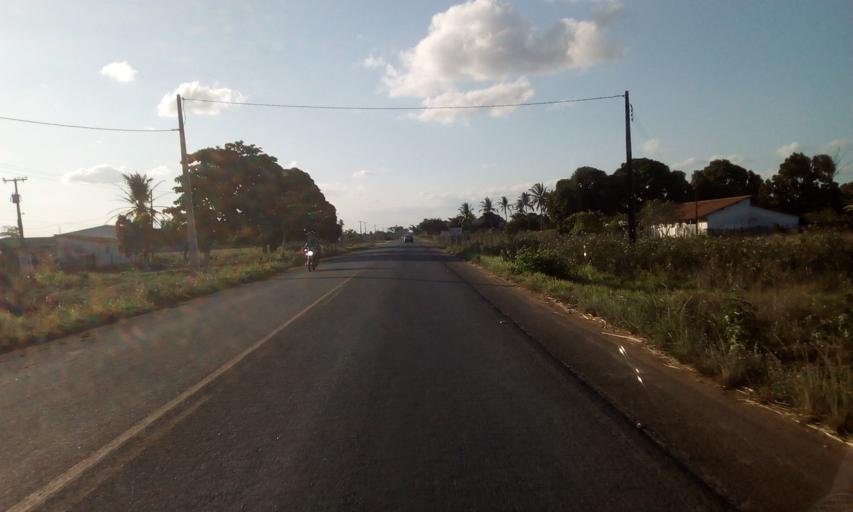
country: BR
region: Paraiba
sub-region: Mari
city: Mari
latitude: -7.0816
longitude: -35.2495
